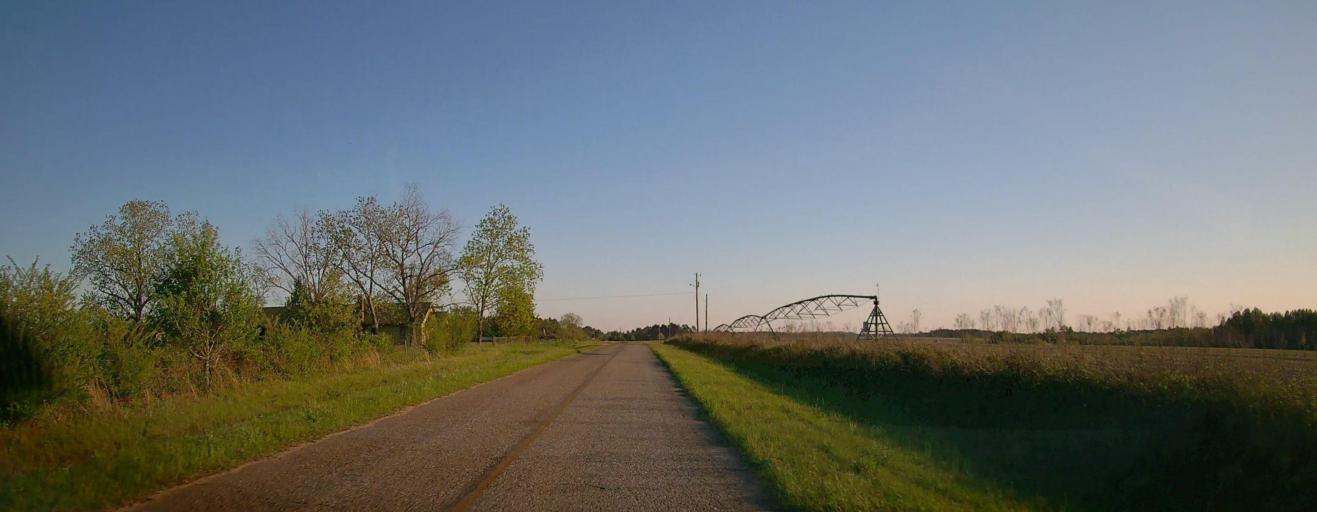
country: US
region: Georgia
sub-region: Ben Hill County
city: Fitzgerald
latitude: 31.6618
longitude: -83.2104
